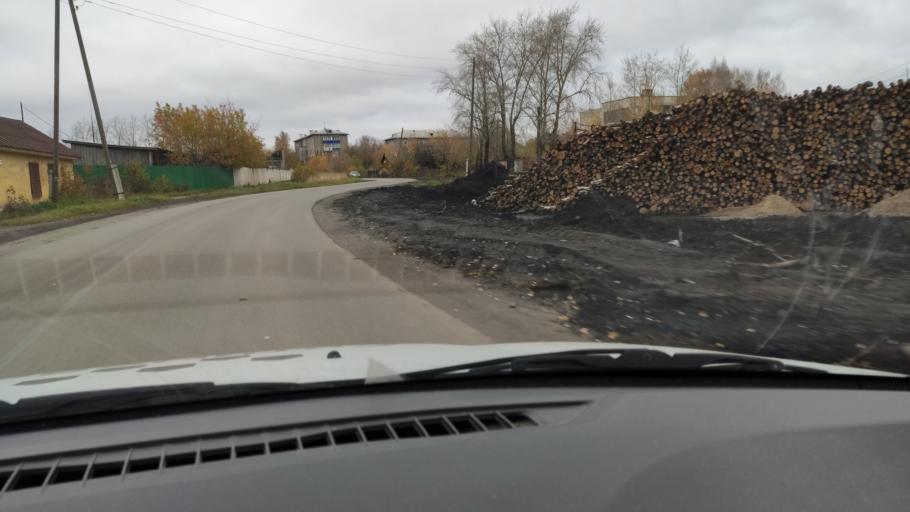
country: RU
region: Kirov
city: Slobodskoy
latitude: 58.7219
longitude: 50.1745
